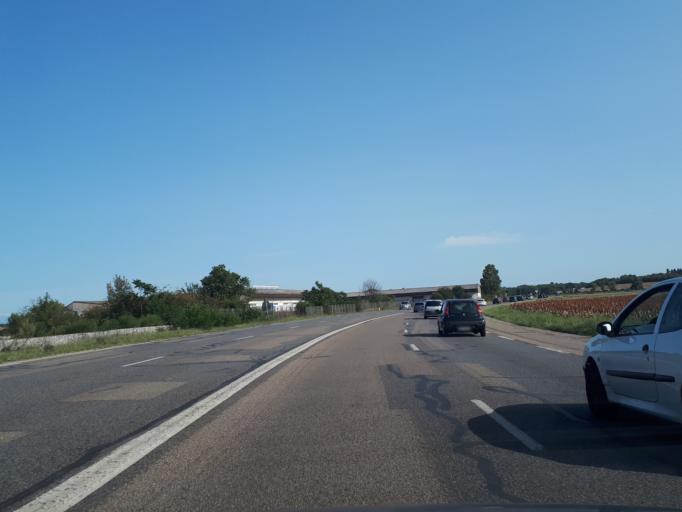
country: FR
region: Rhone-Alpes
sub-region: Departement du Rhone
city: Bron
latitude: 45.7230
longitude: 4.9392
